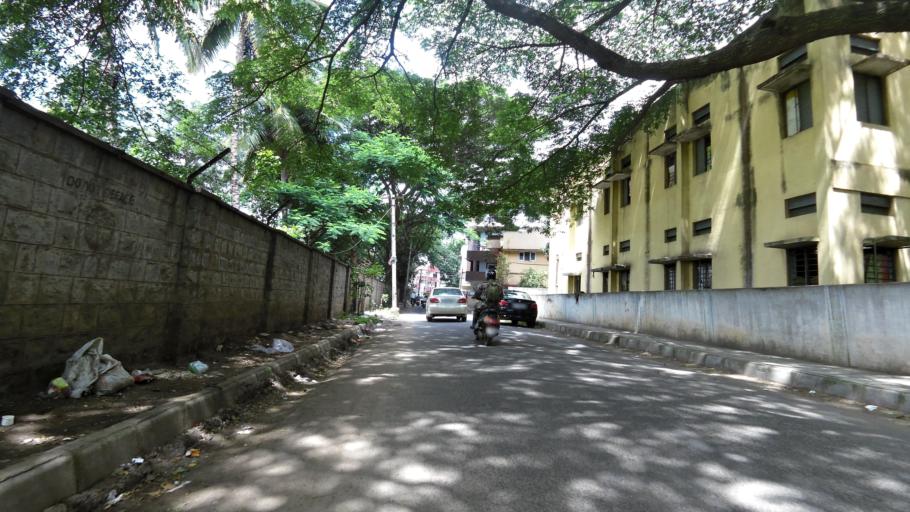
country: IN
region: Karnataka
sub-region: Bangalore Urban
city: Bangalore
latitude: 12.9941
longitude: 77.6287
